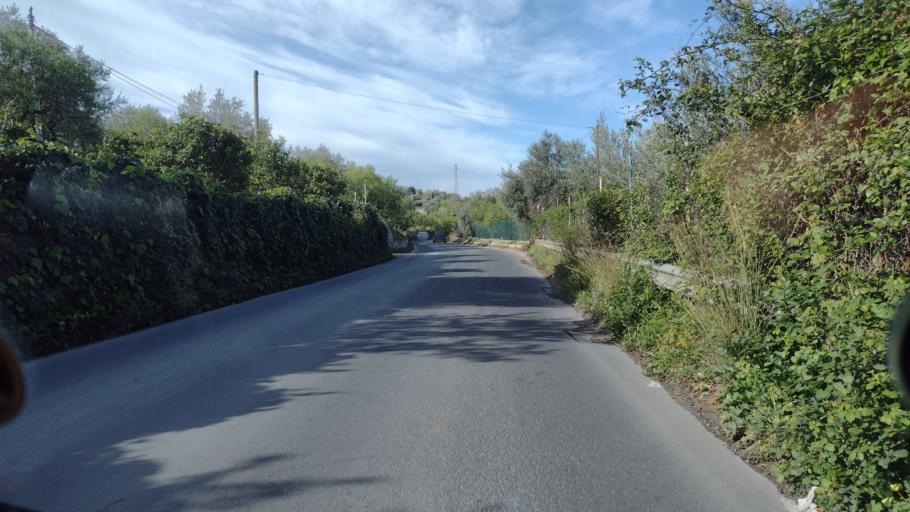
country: IT
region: Sicily
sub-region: Provincia di Siracusa
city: Noto
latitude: 36.8773
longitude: 15.0873
